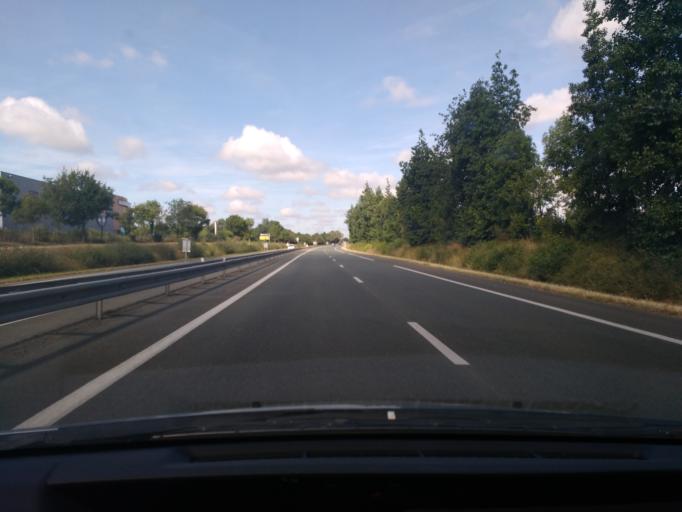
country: FR
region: Pays de la Loire
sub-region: Departement de Maine-et-Loire
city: Saint-Lambert-la-Potherie
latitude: 47.4657
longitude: -0.6673
